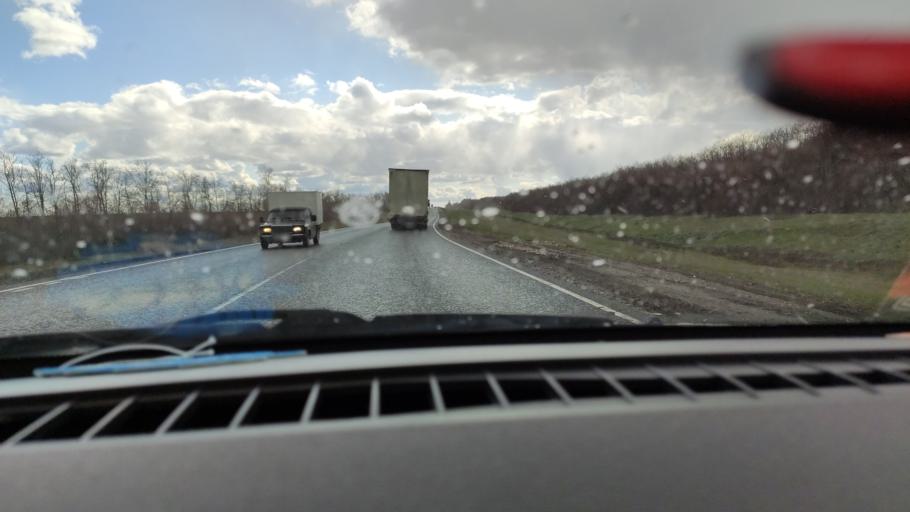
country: RU
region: Saratov
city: Balakovo
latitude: 52.1040
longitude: 47.7402
